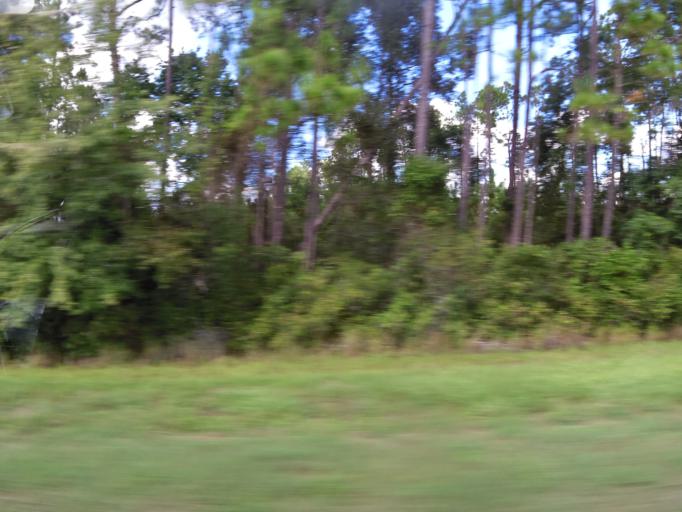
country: US
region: Georgia
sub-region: Echols County
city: Statenville
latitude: 30.6989
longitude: -82.9441
